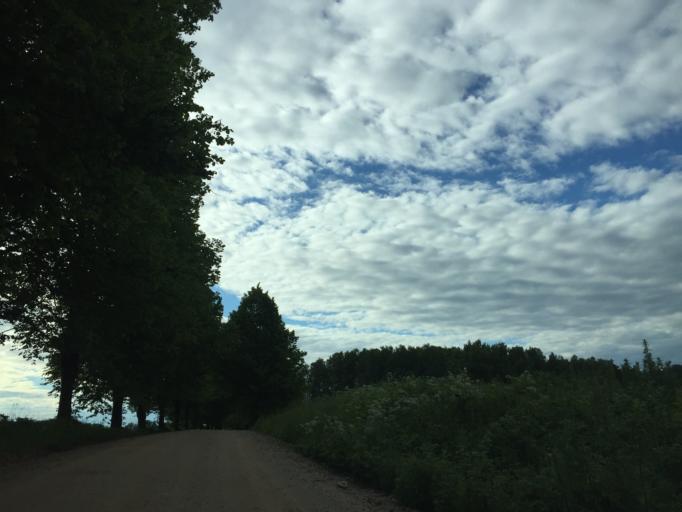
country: LV
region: Amatas Novads
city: Drabesi
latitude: 57.2537
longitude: 25.1706
